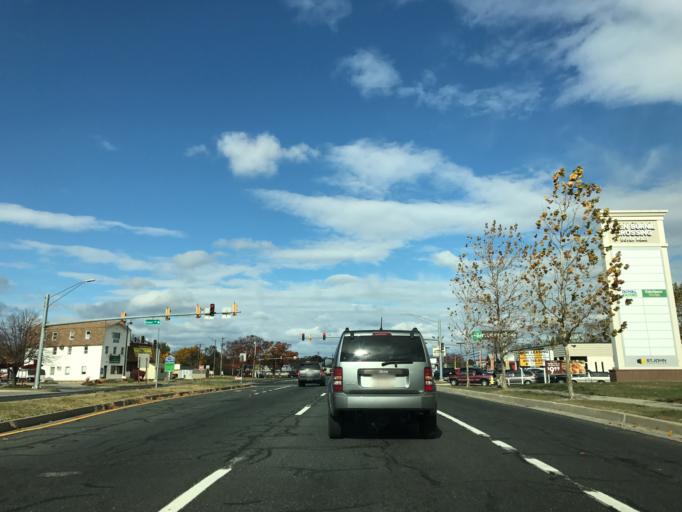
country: US
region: Maryland
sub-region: Anne Arundel County
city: Glen Burnie
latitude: 39.1864
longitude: -76.6127
